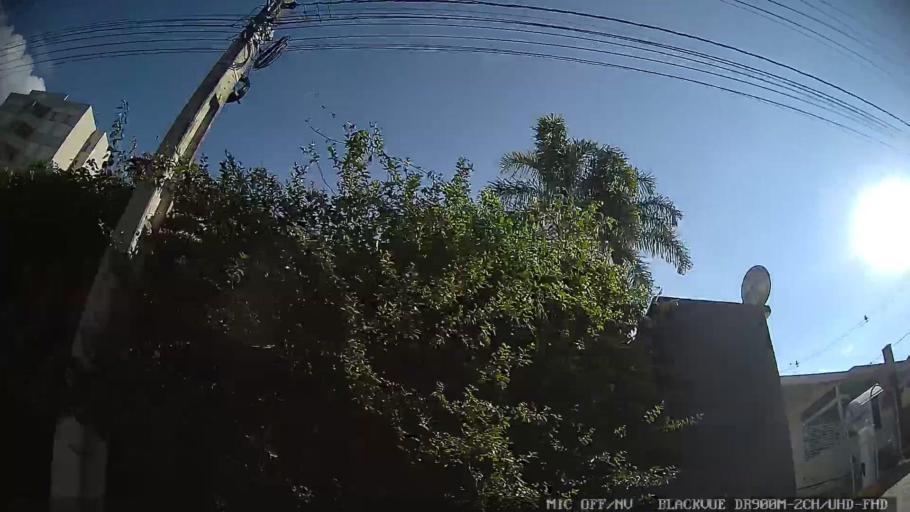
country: BR
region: Sao Paulo
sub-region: Braganca Paulista
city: Braganca Paulista
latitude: -22.9630
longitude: -46.5224
